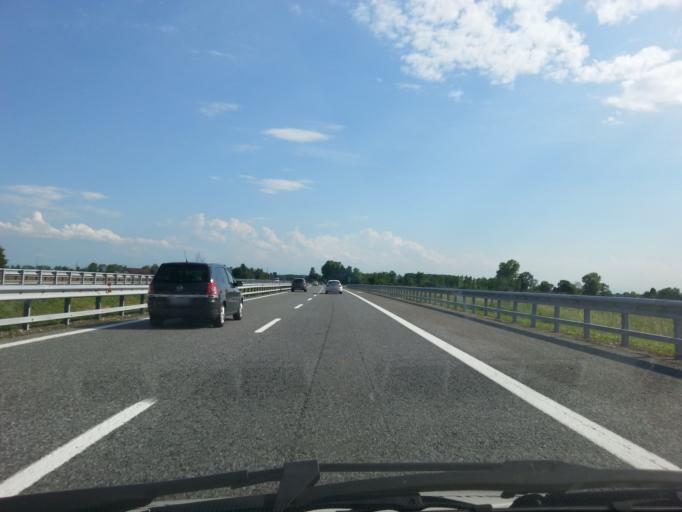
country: IT
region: Piedmont
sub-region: Provincia di Cuneo
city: Caramagna Piemonte
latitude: 44.7572
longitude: 7.7499
